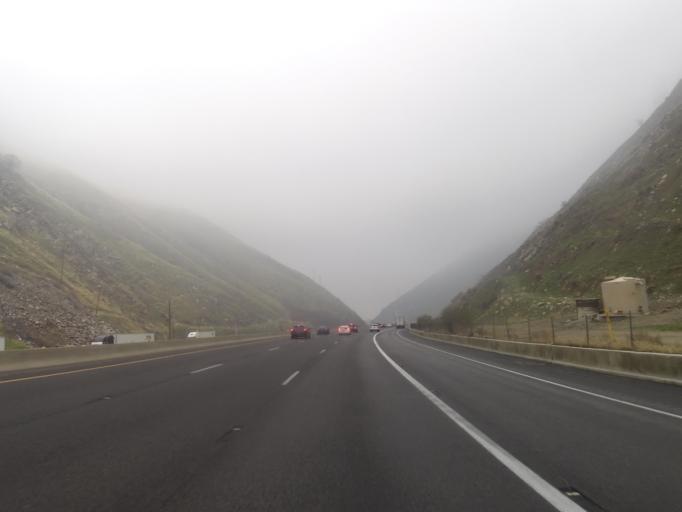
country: US
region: California
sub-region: Kern County
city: Frazier Park
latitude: 34.9070
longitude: -118.9235
